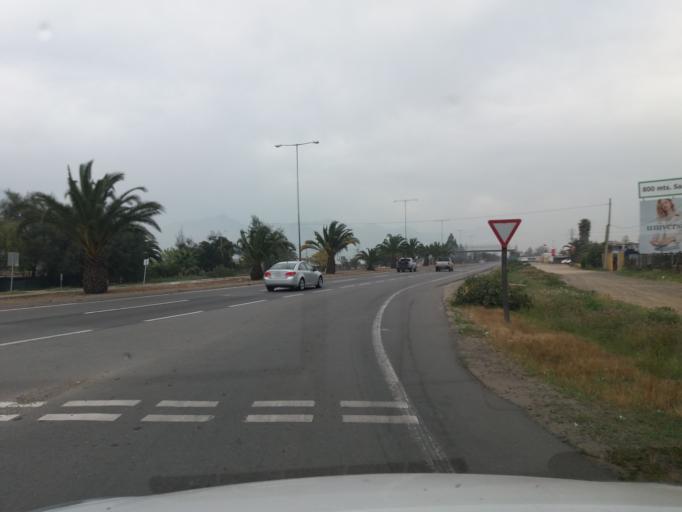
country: CL
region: Valparaiso
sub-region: Provincia de Quillota
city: Hacienda La Calera
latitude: -32.7725
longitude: -71.1876
